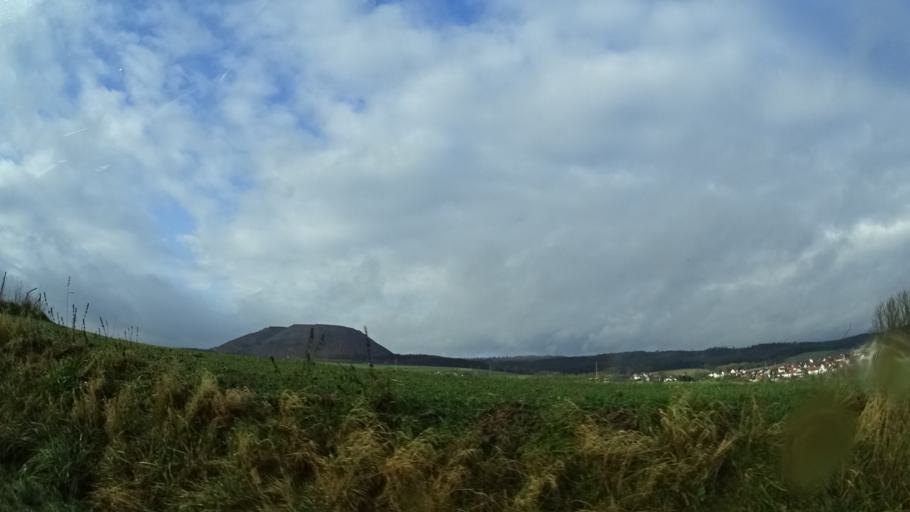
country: DE
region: Hesse
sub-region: Regierungsbezirk Kassel
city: Neuhof
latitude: 50.4568
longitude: 9.6270
